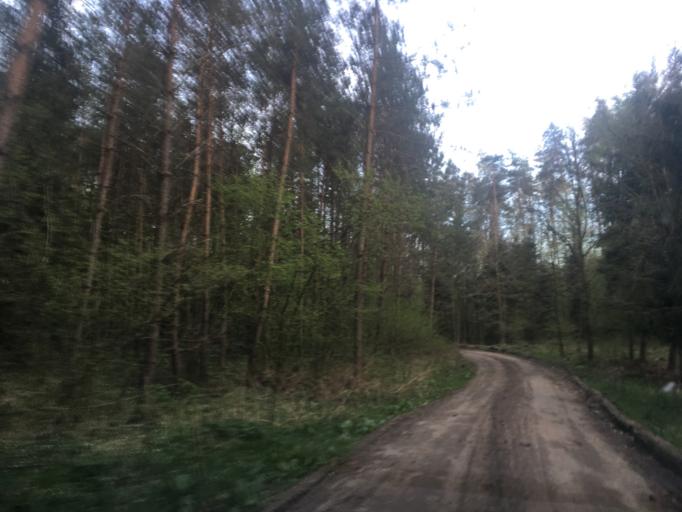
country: PL
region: Kujawsko-Pomorskie
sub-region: Powiat brodnicki
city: Gorzno
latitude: 53.2044
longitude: 19.6793
